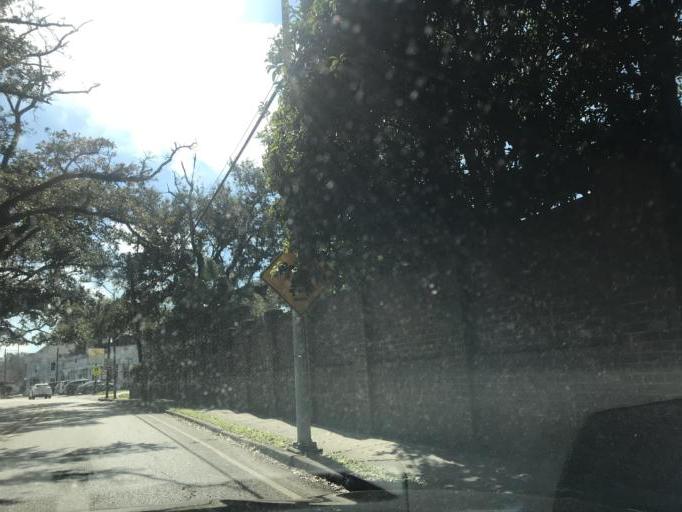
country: US
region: Louisiana
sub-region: Jefferson Parish
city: Metairie
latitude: 29.9818
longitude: -90.1279
